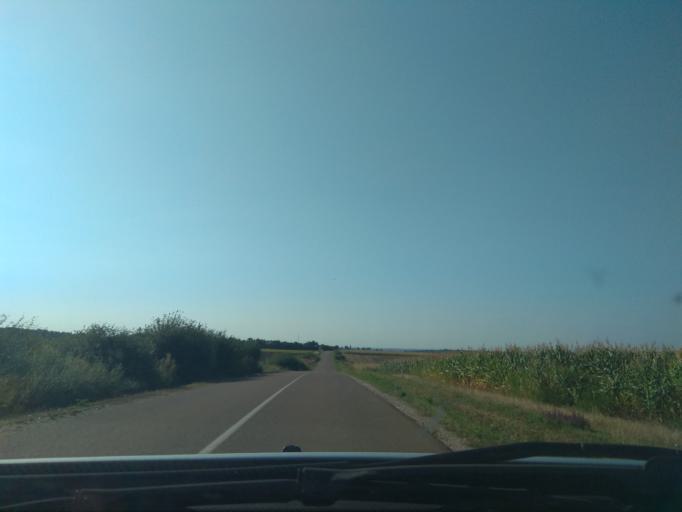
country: HU
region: Borsod-Abauj-Zemplen
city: Emod
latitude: 47.9665
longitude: 20.8002
